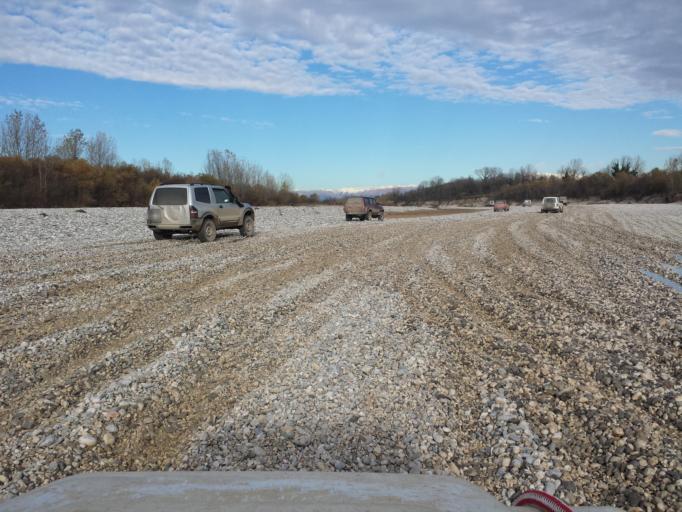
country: IT
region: Friuli Venezia Giulia
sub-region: Provincia di Udine
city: San Vito al Torre
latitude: 45.9101
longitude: 13.3878
